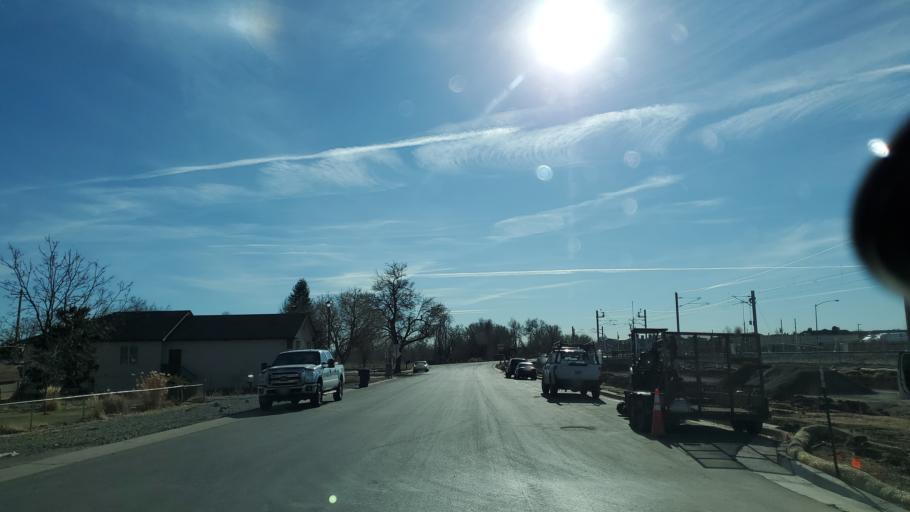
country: US
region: Colorado
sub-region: Adams County
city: Northglenn
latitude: 39.9223
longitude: -104.9613
